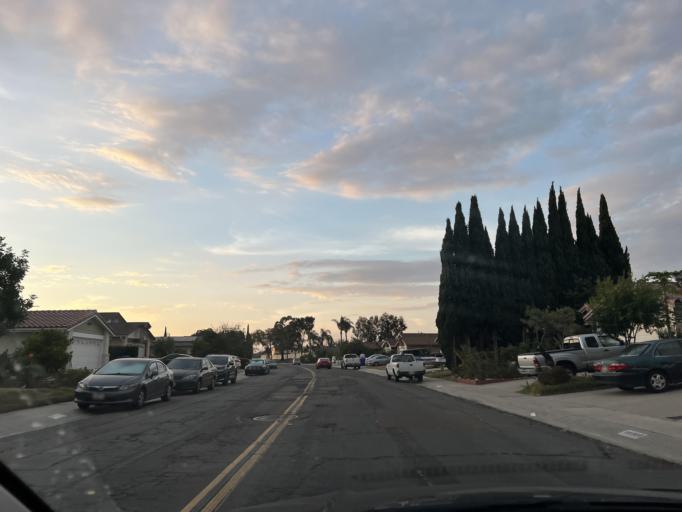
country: US
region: California
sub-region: San Diego County
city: Fairbanks Ranch
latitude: 32.9083
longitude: -117.1545
